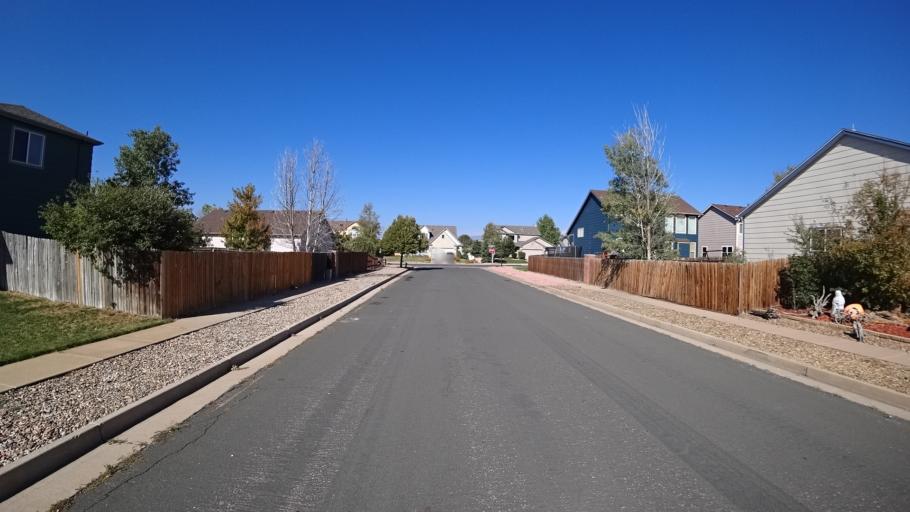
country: US
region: Colorado
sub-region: El Paso County
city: Cimarron Hills
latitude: 38.8800
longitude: -104.7071
